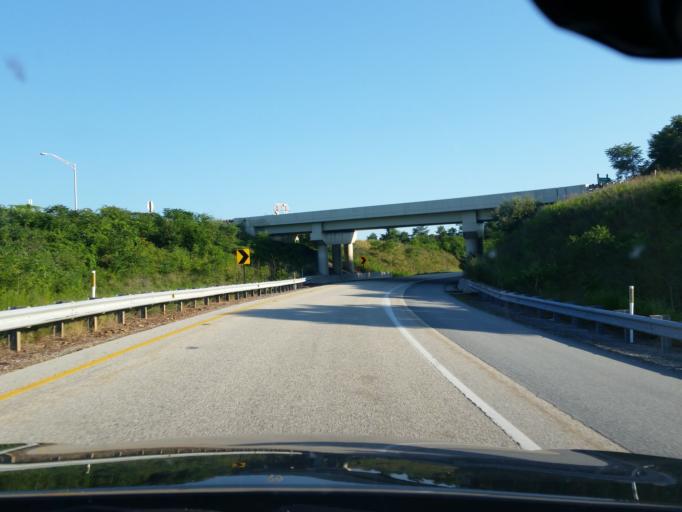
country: US
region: Pennsylvania
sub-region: Perry County
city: Marysville
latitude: 40.3701
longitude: -76.9425
